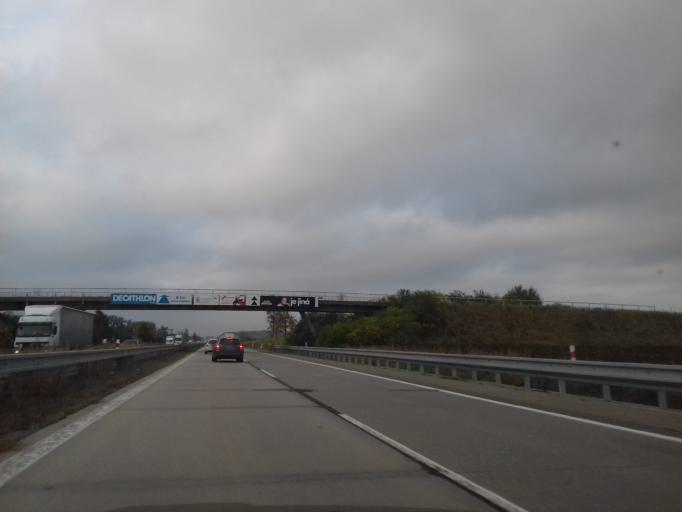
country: CZ
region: South Moravian
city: Rajhradice
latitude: 49.0846
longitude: 16.6585
